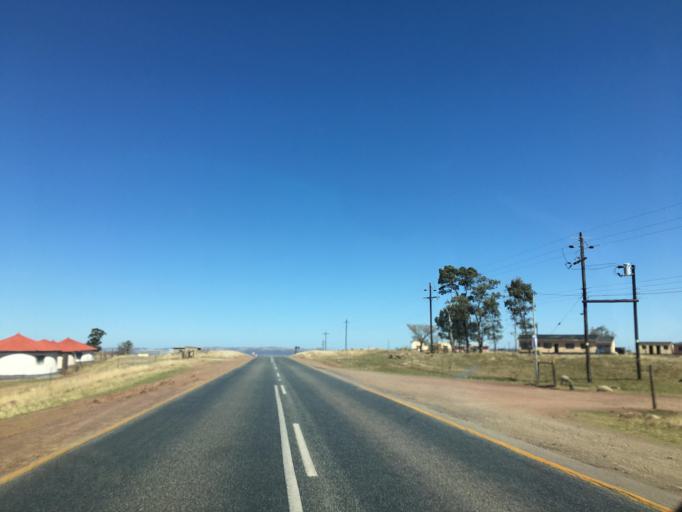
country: ZA
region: Eastern Cape
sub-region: Chris Hani District Municipality
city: Cofimvaba
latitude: -31.9371
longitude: 27.8373
